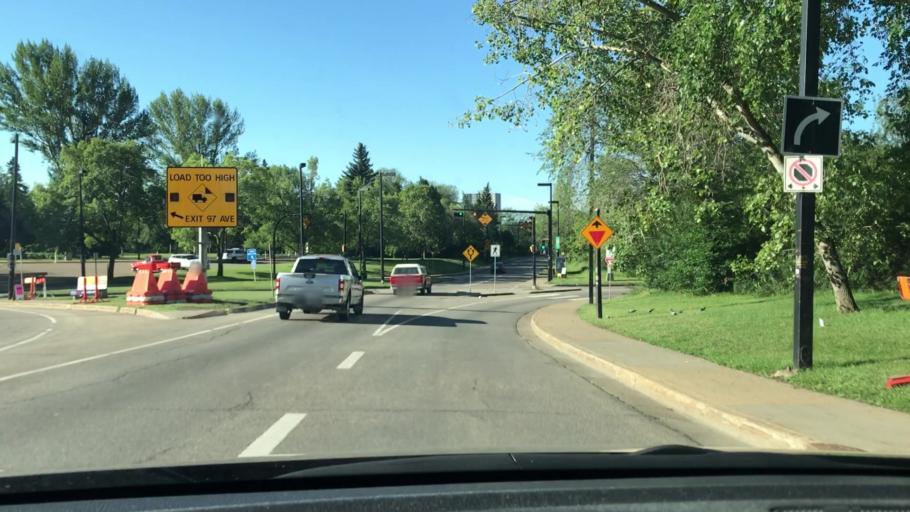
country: CA
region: Alberta
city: Edmonton
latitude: 53.5347
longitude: -113.5087
